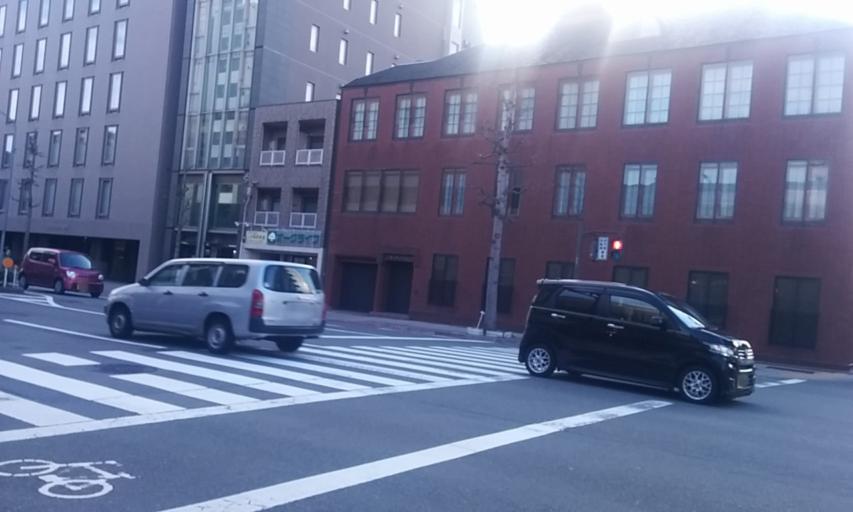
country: JP
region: Kyoto
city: Kyoto
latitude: 35.0136
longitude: 135.7597
